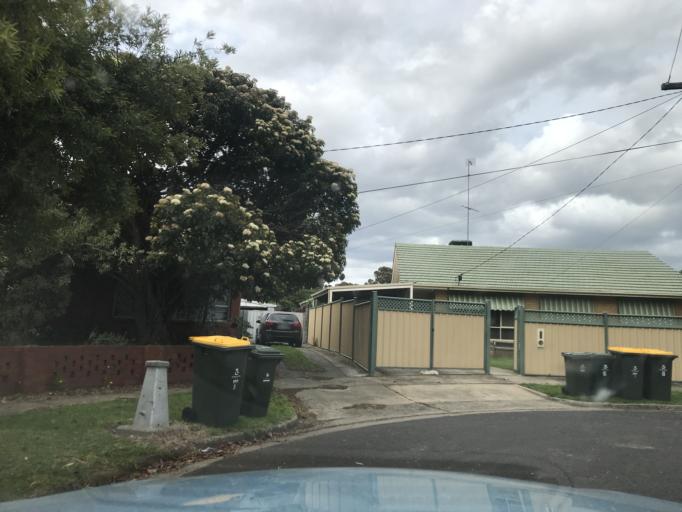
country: AU
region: Victoria
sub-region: Hobsons Bay
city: Laverton
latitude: -37.8511
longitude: 144.7763
